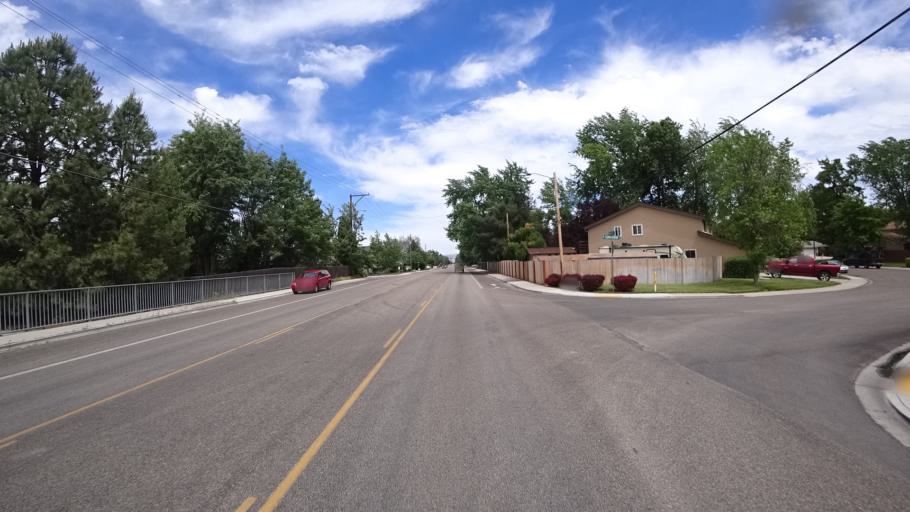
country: US
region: Idaho
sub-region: Ada County
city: Eagle
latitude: 43.6384
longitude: -116.3143
